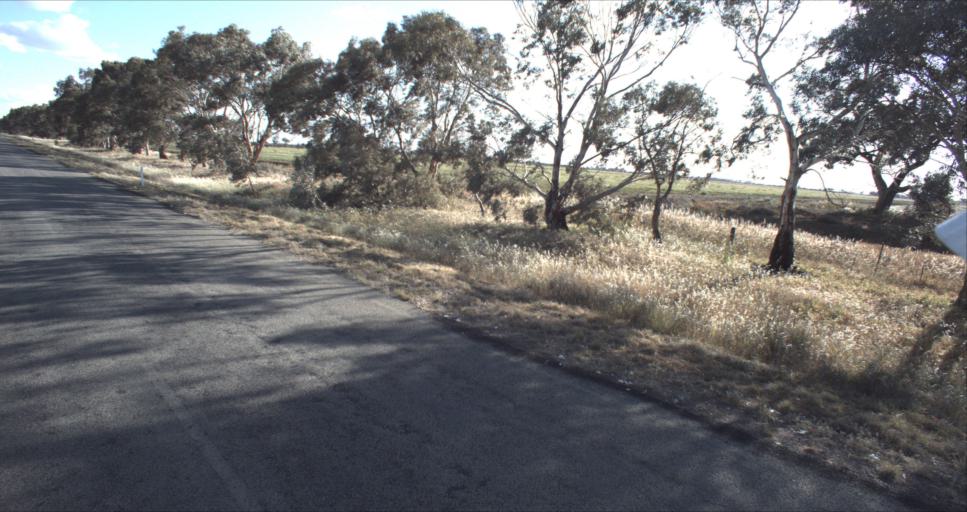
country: AU
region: New South Wales
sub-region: Leeton
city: Leeton
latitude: -34.5423
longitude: 146.2798
